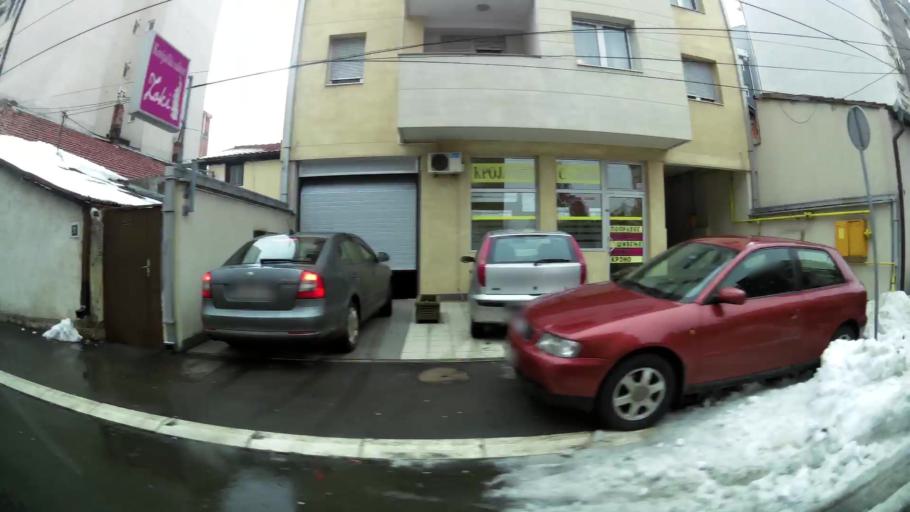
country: RS
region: Central Serbia
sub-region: Belgrade
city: Vozdovac
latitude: 44.7733
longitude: 20.4777
